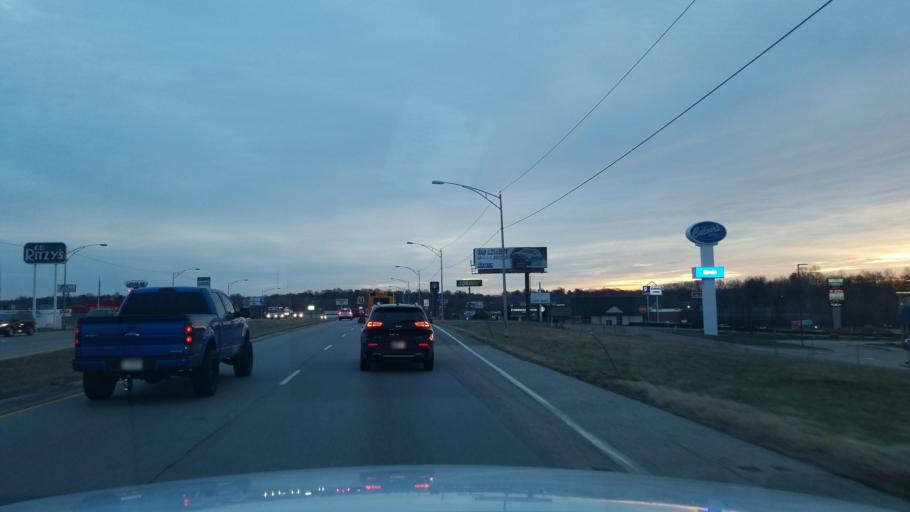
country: US
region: Indiana
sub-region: Vanderburgh County
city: Evansville
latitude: 37.9767
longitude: -87.6351
